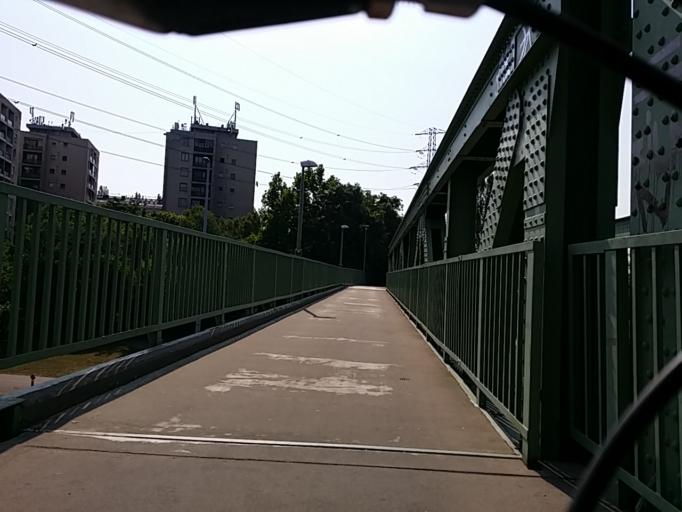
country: HU
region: Budapest
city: Budapest IV. keruelet
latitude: 47.5605
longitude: 19.0769
